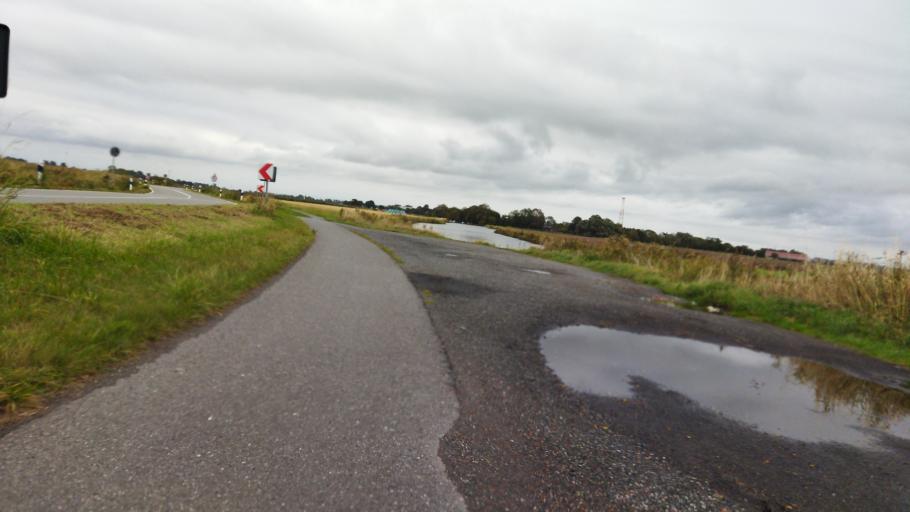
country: DE
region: Lower Saxony
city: Wirdum
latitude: 53.4943
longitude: 7.1077
